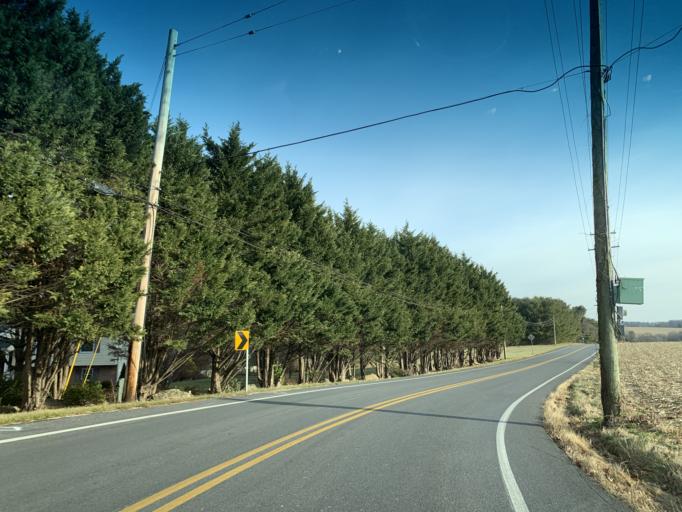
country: US
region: Maryland
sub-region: Carroll County
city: Hampstead
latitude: 39.6114
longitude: -76.8194
